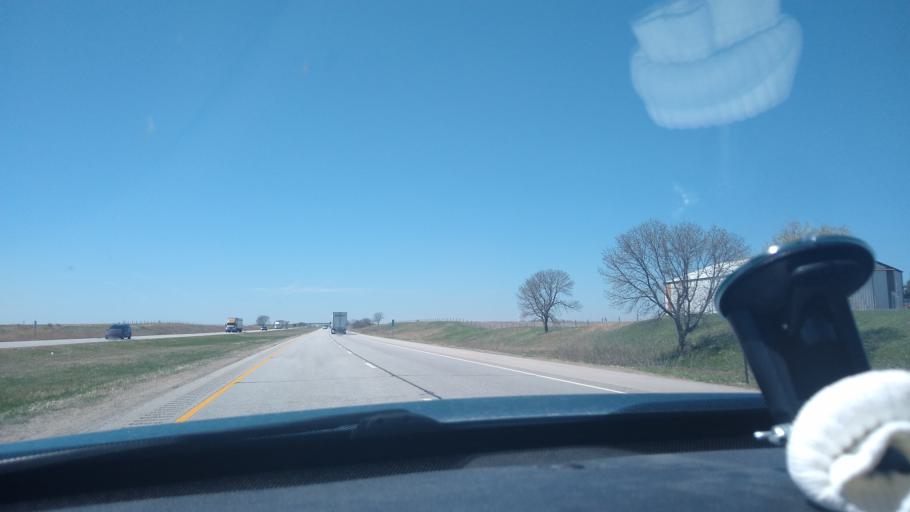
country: US
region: Nebraska
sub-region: York County
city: York
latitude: 40.8213
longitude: -97.4079
